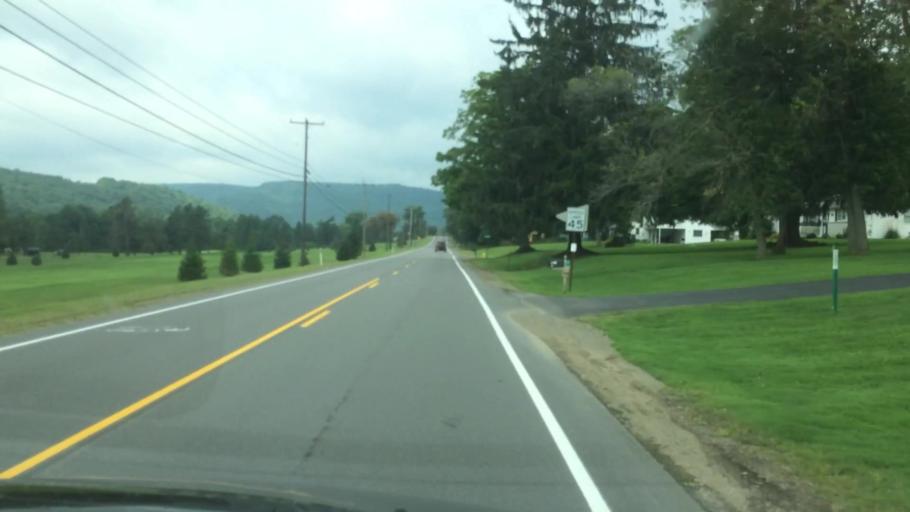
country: US
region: Pennsylvania
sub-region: McKean County
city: Bradford
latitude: 41.9054
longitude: -78.6178
